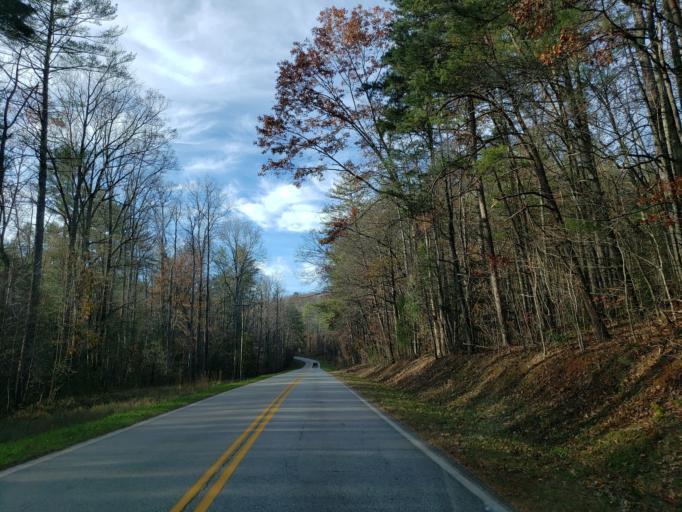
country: US
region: Georgia
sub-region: Lumpkin County
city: Dahlonega
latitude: 34.6266
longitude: -84.0962
